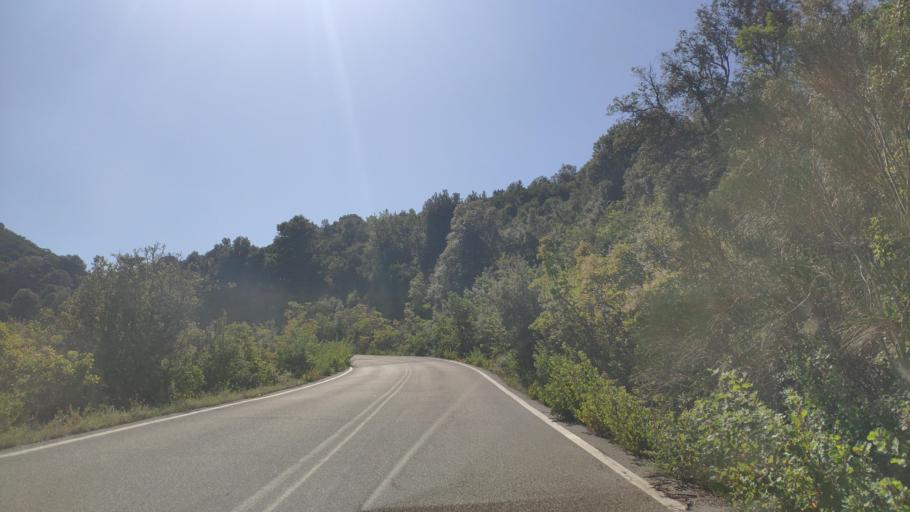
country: GR
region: West Greece
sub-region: Nomos Aitolias kai Akarnanias
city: Sardinia
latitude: 38.9221
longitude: 21.4032
